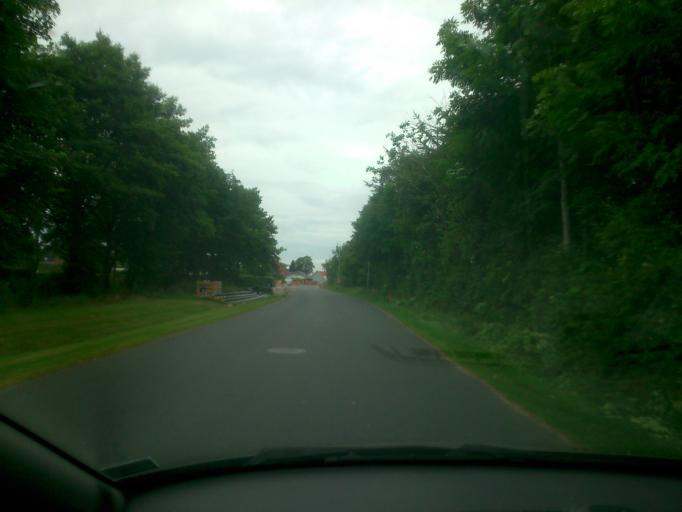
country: DK
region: South Denmark
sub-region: Esbjerg Kommune
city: Esbjerg
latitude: 55.5318
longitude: 8.4422
